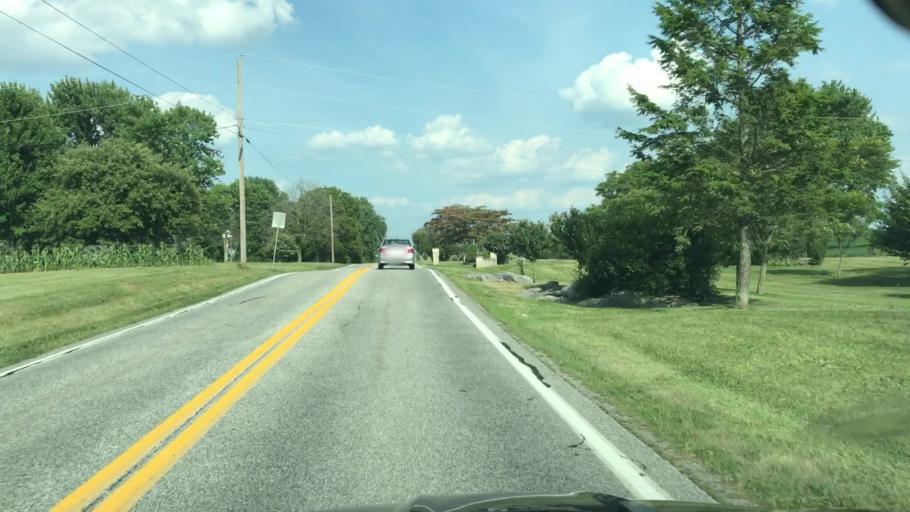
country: US
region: Pennsylvania
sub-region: Cumberland County
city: Boiling Springs
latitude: 40.1812
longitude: -77.0982
